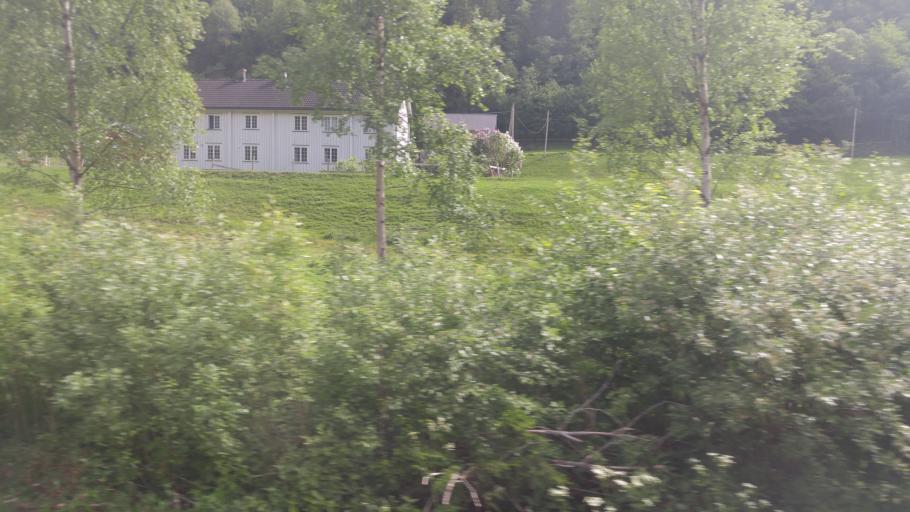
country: NO
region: Sor-Trondelag
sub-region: Midtre Gauldal
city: Storen
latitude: 63.0067
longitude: 10.4570
